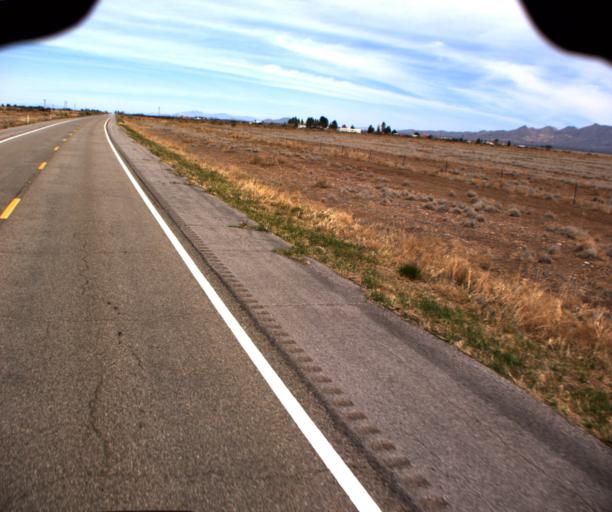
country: US
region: Arizona
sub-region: Cochise County
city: Pirtleville
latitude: 31.5648
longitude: -109.6676
